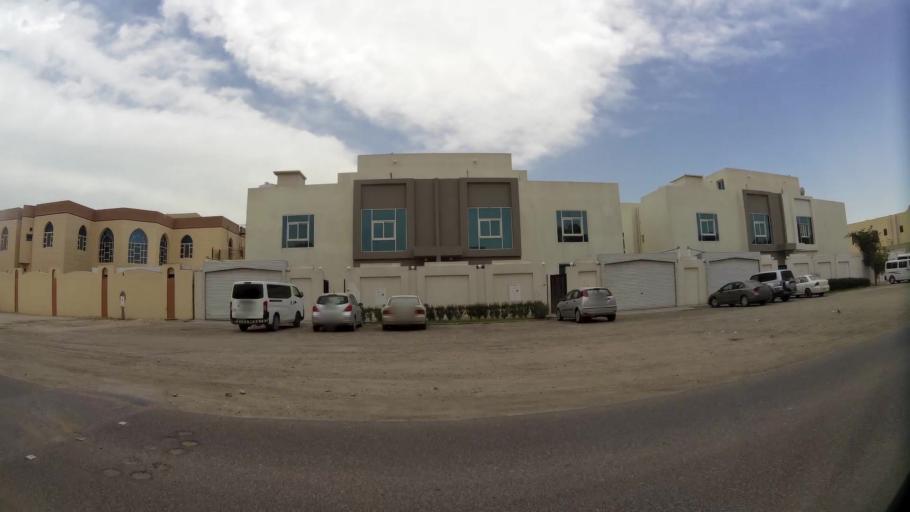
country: QA
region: Baladiyat ar Rayyan
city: Ar Rayyan
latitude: 25.2738
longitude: 51.4398
